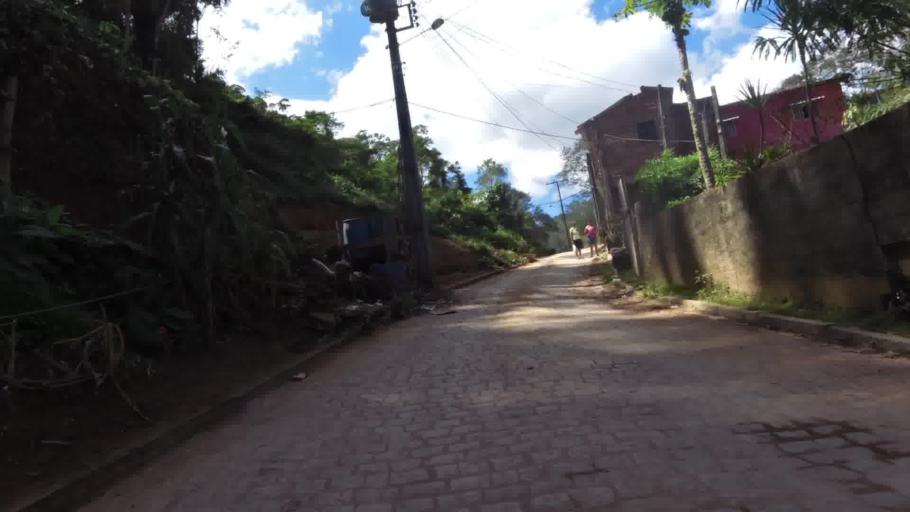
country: BR
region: Espirito Santo
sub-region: Vargem Alta
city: Vargem Alta
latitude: -20.6713
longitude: -41.0015
